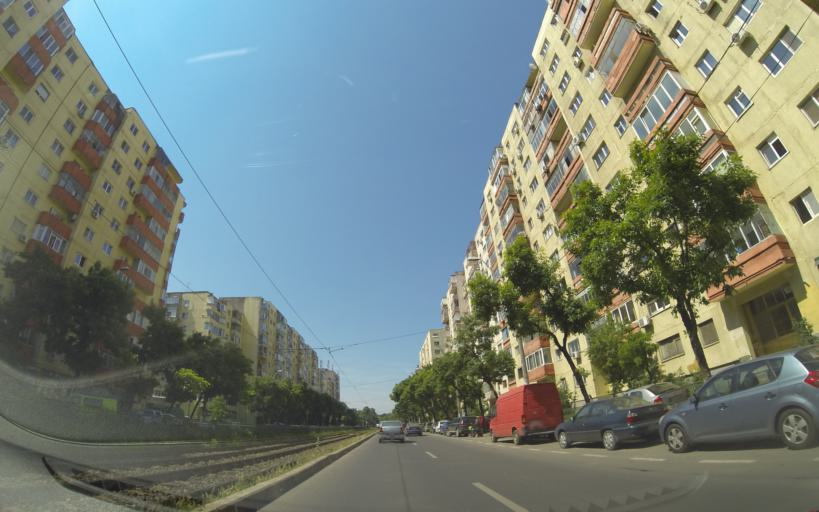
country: RO
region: Bucuresti
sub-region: Municipiul Bucuresti
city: Bucuresti
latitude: 44.4080
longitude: 26.0665
